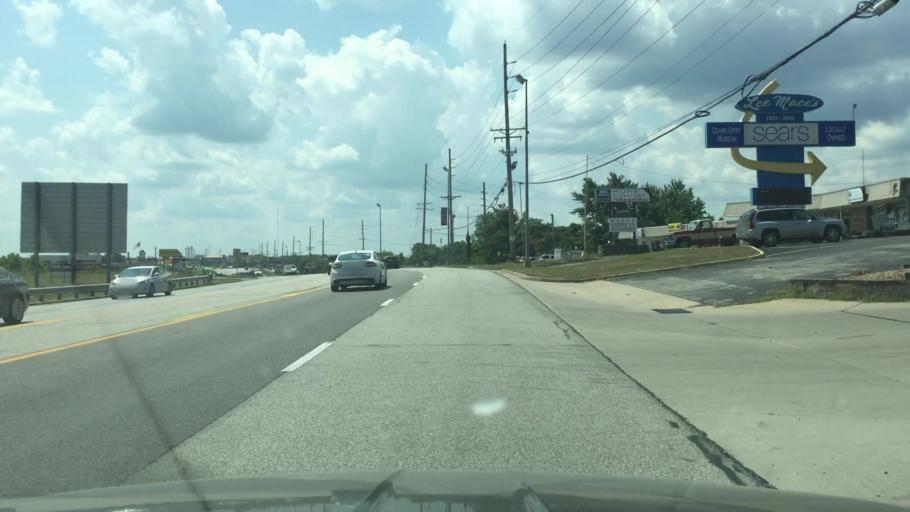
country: US
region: Missouri
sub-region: Miller County
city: Lake Ozark
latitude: 38.1672
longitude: -92.6110
